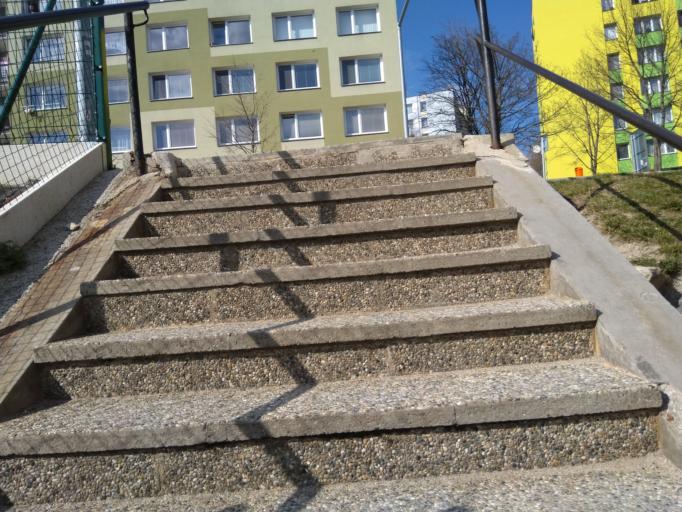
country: CZ
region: Jihocesky
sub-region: Okres Prachatice
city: Vimperk
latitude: 49.0610
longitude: 13.7797
